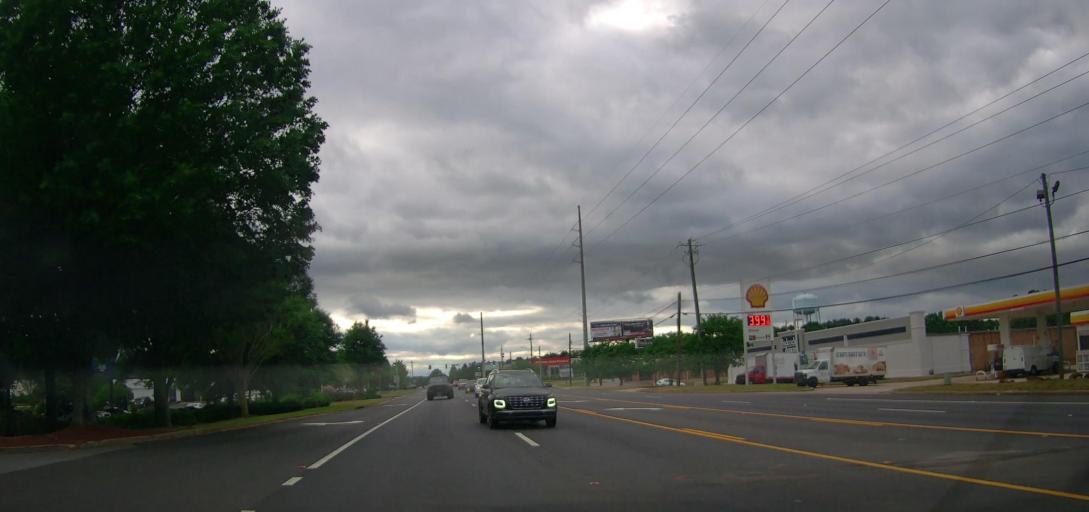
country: US
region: Georgia
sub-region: Oconee County
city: Bogart
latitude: 33.9402
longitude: -83.4859
